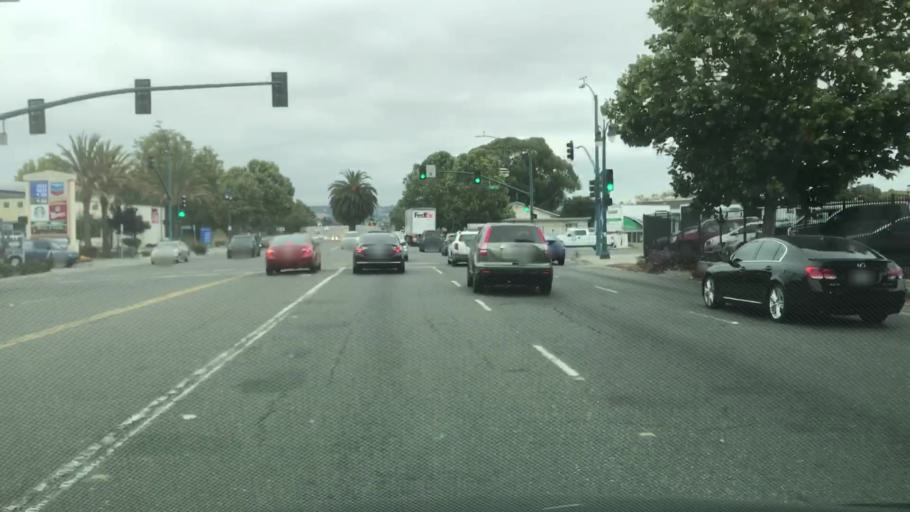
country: US
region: California
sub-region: Alameda County
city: San Leandro
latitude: 37.7289
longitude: -122.1954
